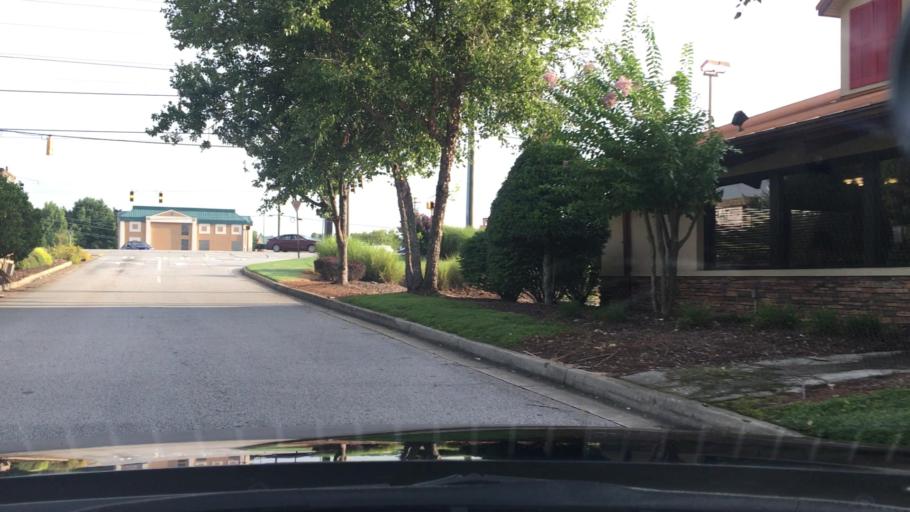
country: US
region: Georgia
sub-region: Coweta County
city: Newnan
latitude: 33.3958
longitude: -84.7584
